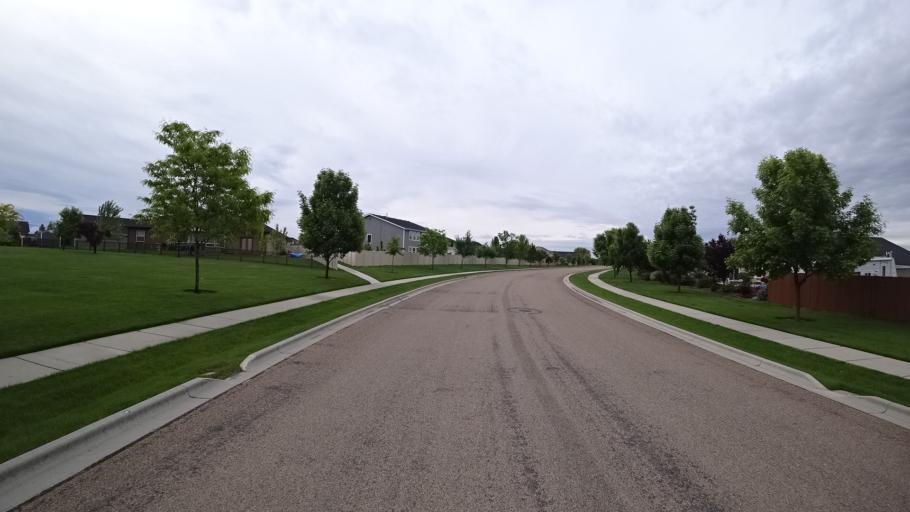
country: US
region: Idaho
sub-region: Ada County
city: Star
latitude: 43.7002
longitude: -116.5052
